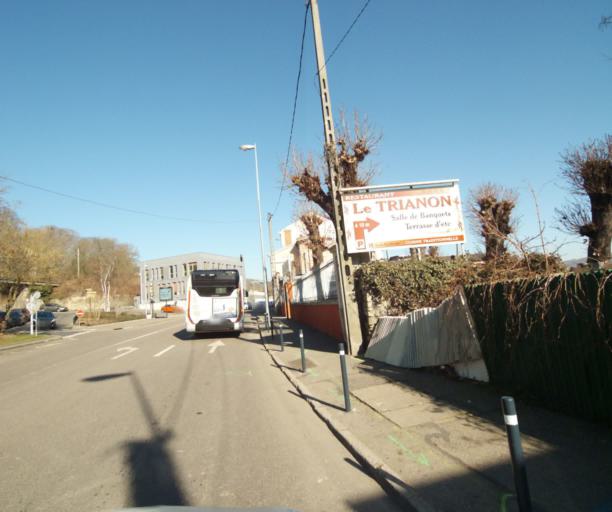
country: FR
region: Lorraine
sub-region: Departement de Meurthe-et-Moselle
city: Maxeville
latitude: 48.7072
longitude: 6.1669
